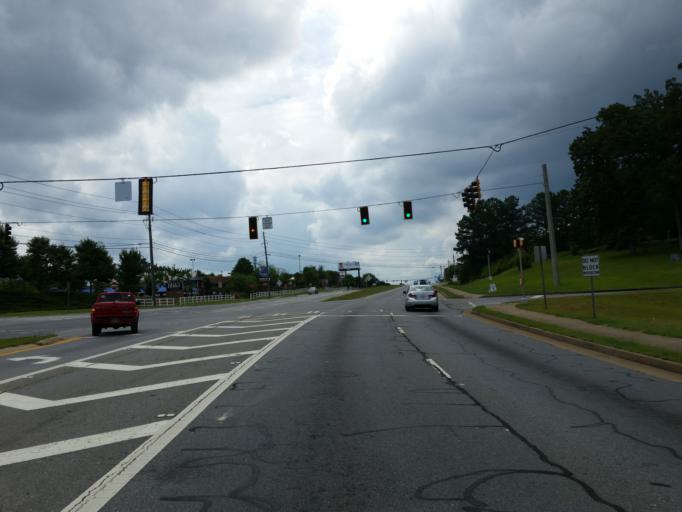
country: US
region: Georgia
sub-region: Cherokee County
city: Woodstock
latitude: 34.0873
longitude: -84.4786
